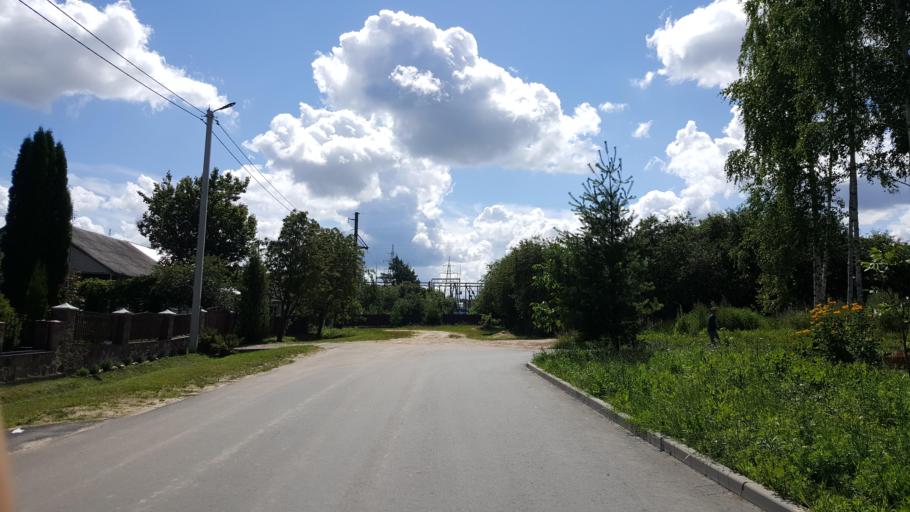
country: BY
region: Brest
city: Kamyanyets
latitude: 52.3914
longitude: 23.8334
